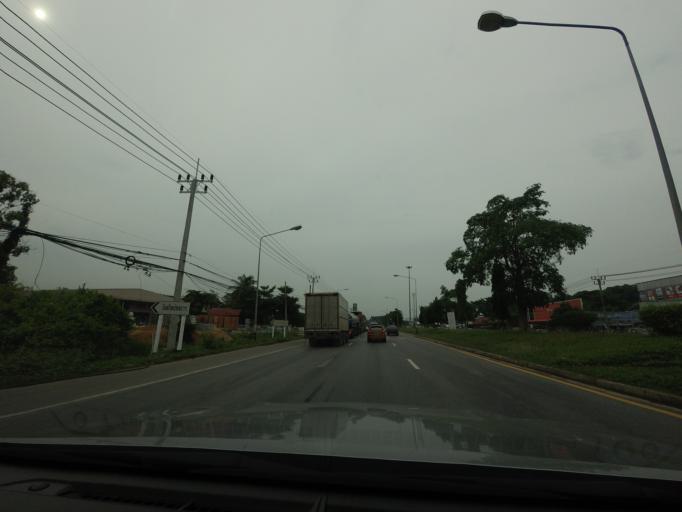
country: TH
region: Songkhla
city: Ban Mai
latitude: 7.2134
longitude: 100.5567
